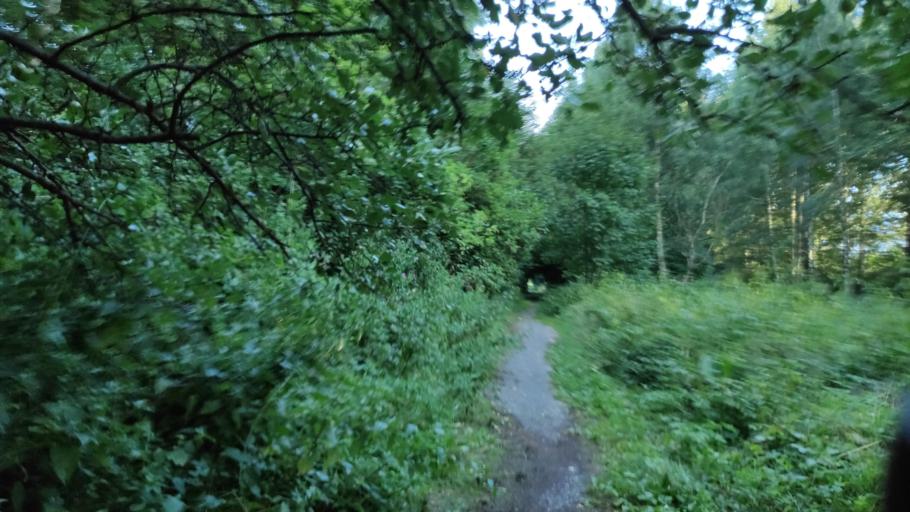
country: SK
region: Zilinsky
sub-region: Okres Liptovsky Mikulas
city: Liptovsky Mikulas
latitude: 49.0798
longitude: 19.5892
